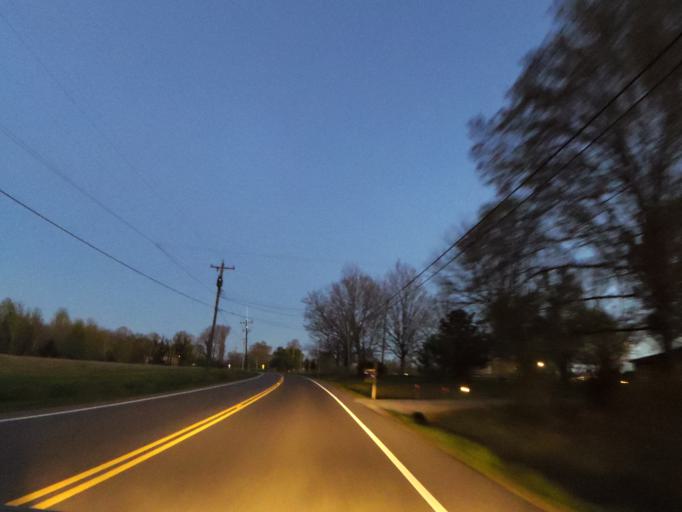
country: US
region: Tennessee
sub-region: Robertson County
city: Greenbrier
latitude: 36.3606
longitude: -86.8859
